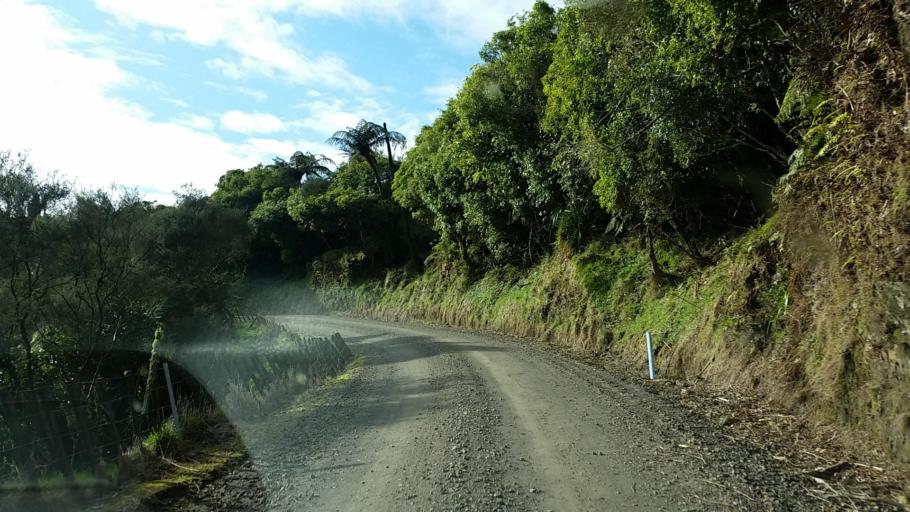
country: NZ
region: Taranaki
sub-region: South Taranaki District
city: Eltham
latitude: -39.1752
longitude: 174.6280
